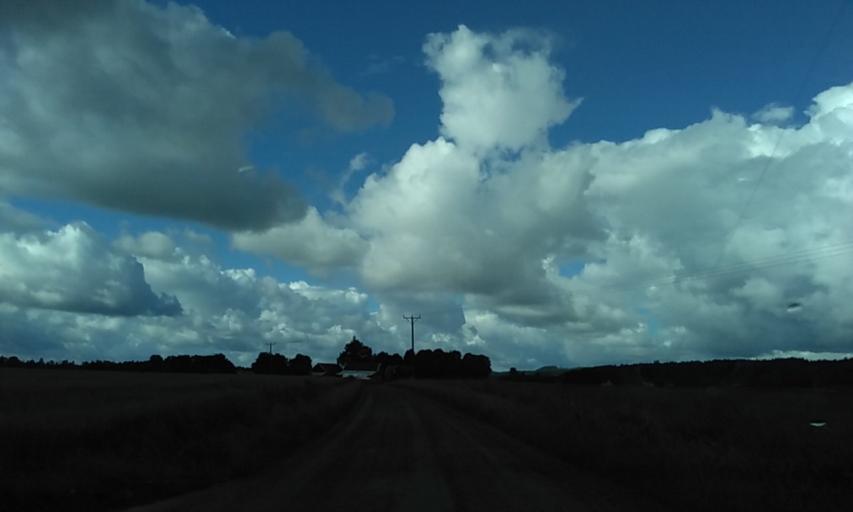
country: SE
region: Vaestra Goetaland
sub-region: Vargarda Kommun
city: Jonstorp
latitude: 57.9905
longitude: 12.6163
